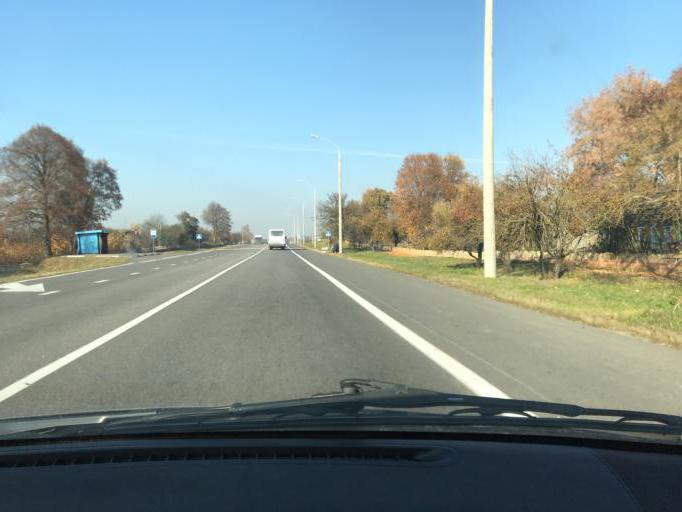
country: BY
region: Mogilev
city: Shklow
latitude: 54.3116
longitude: 30.4476
